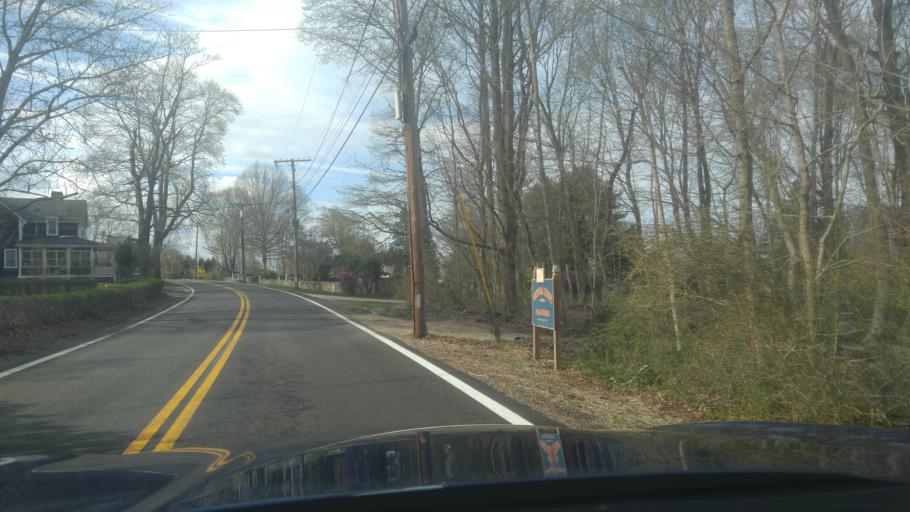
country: US
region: Rhode Island
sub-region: Newport County
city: Jamestown
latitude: 41.5685
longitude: -71.3650
